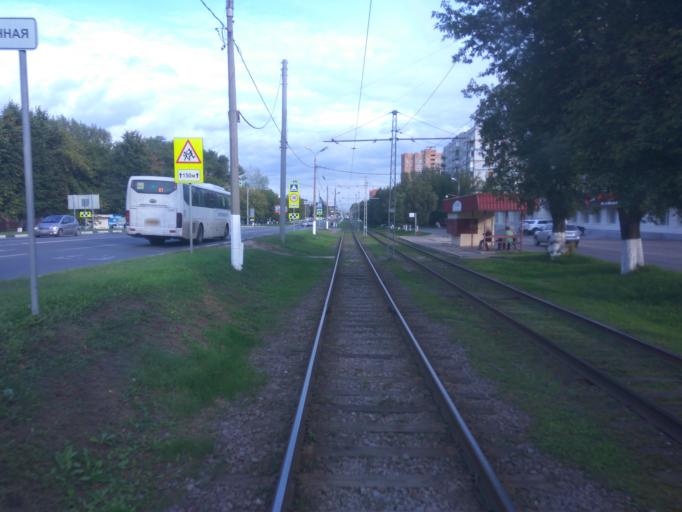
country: RU
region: Moskovskaya
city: Kolomna
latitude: 55.0878
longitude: 38.7899
